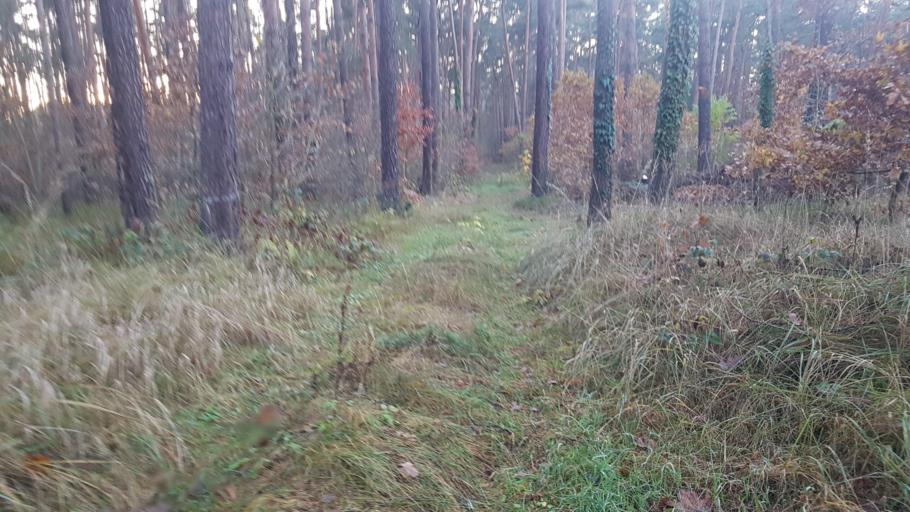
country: DE
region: Brandenburg
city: Merzdorf
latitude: 51.3966
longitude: 13.5360
